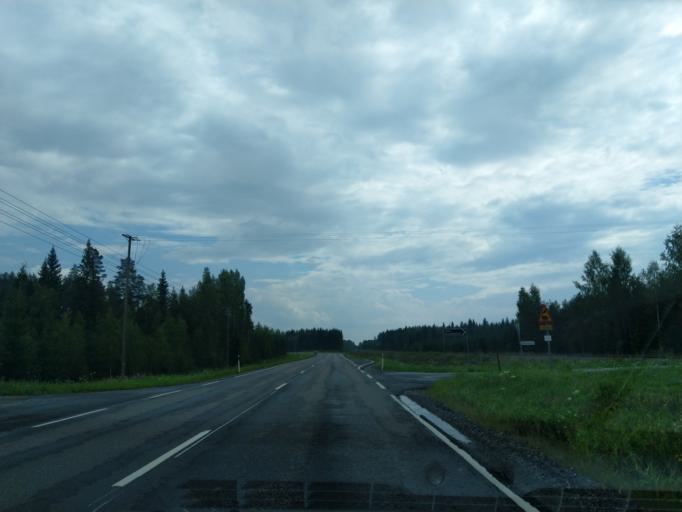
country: FI
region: South Karelia
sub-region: Imatra
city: Parikkala
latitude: 61.6295
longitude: 29.4321
